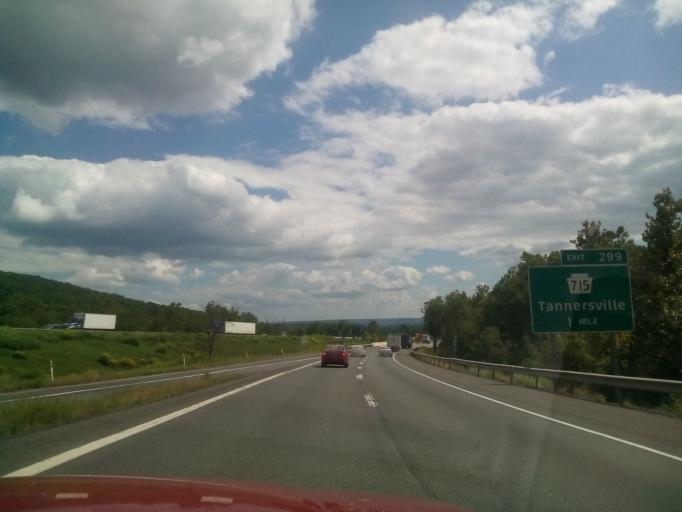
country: US
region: Pennsylvania
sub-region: Monroe County
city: Tannersville
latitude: 41.0534
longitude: -75.3177
